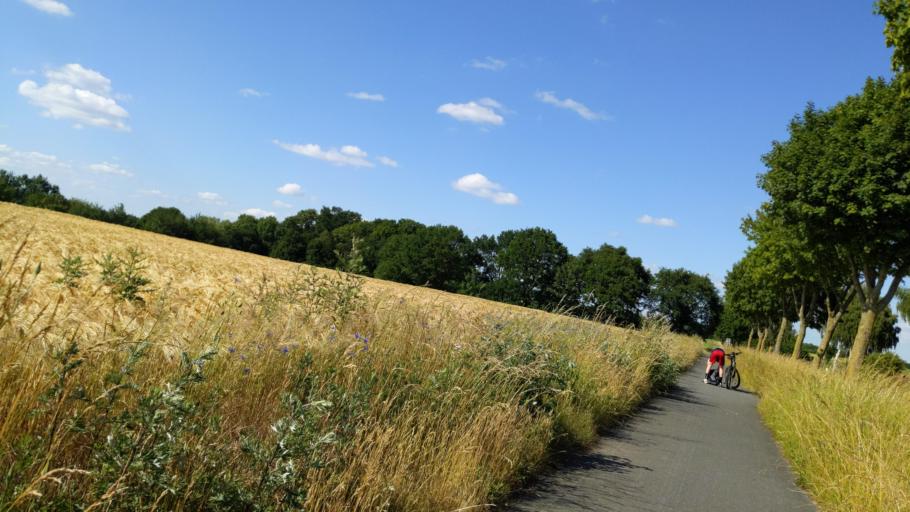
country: DE
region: Schleswig-Holstein
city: Berkenthin
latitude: 53.7206
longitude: 10.6483
